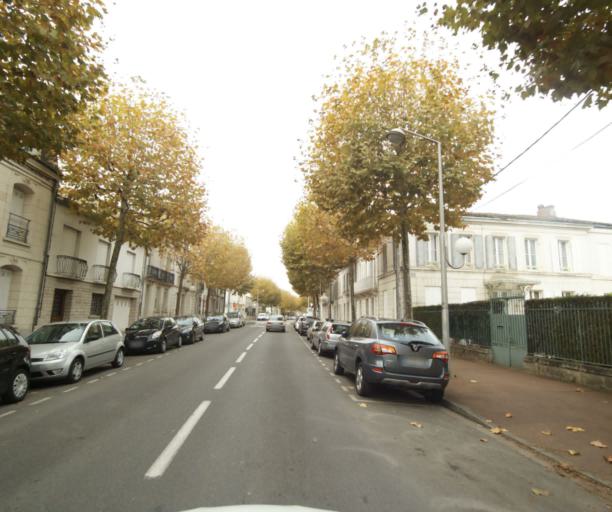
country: FR
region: Poitou-Charentes
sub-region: Departement de la Charente-Maritime
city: Saintes
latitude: 45.7478
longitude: -0.6412
